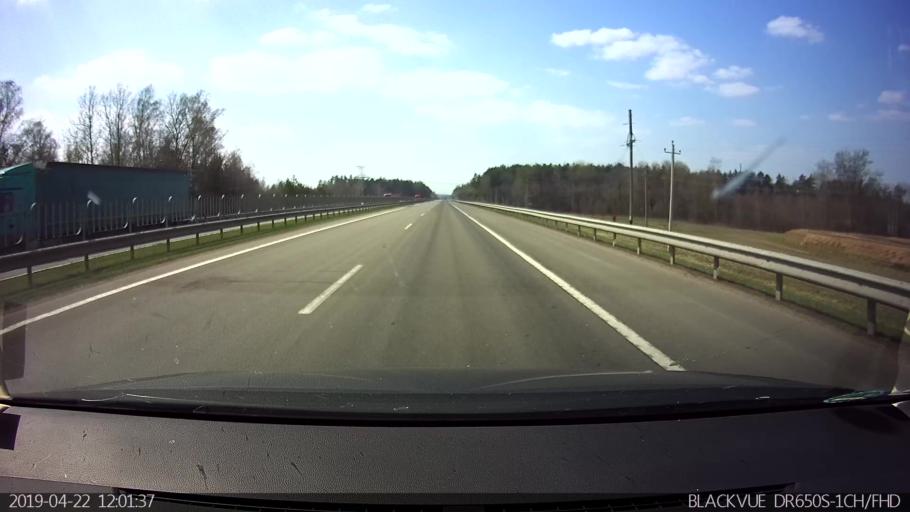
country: BY
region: Minsk
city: Pryvol'ny
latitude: 53.8002
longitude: 27.7779
